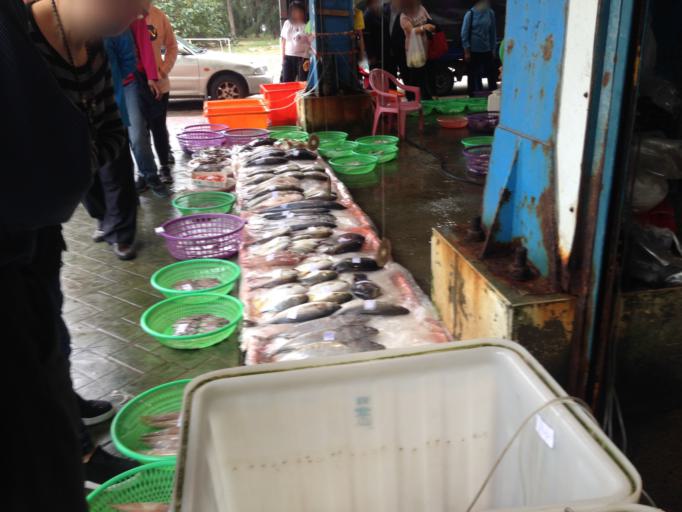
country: TW
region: Taiwan
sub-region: Miaoli
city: Miaoli
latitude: 24.6996
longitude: 120.8592
